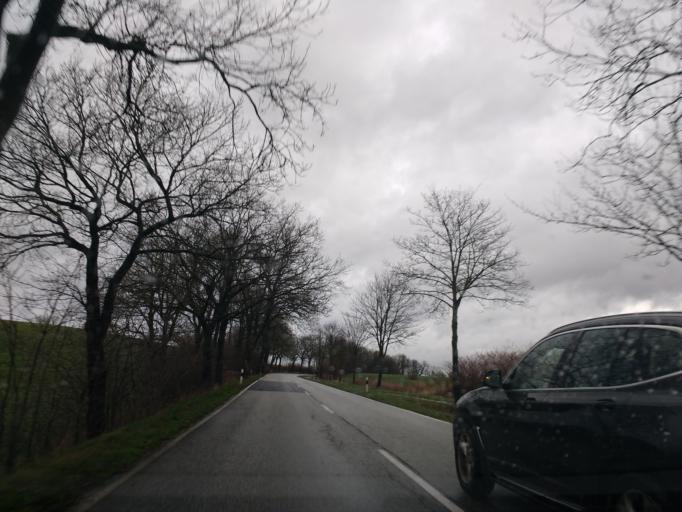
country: DE
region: Schleswig-Holstein
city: Blekendorf
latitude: 54.2893
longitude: 10.7107
